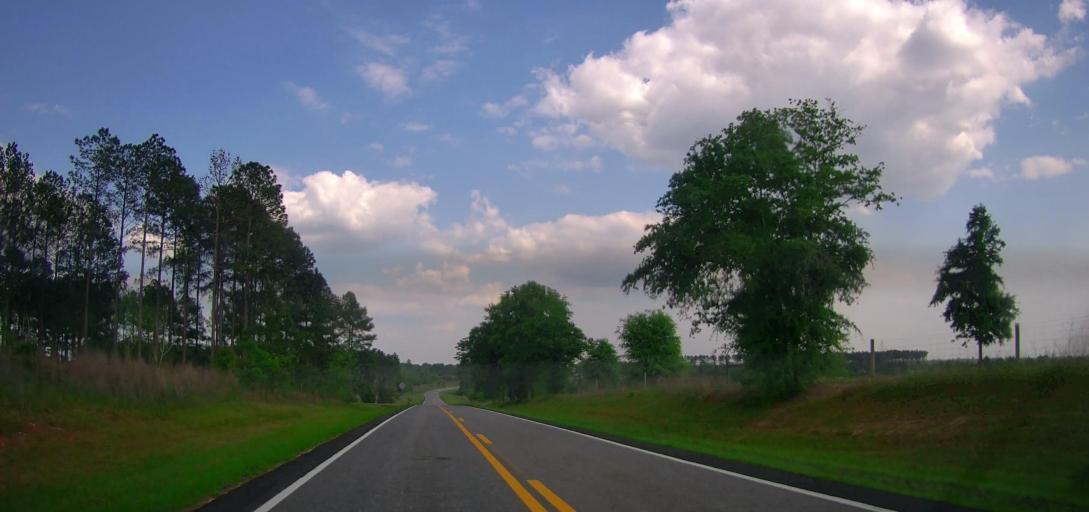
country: US
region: Georgia
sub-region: Laurens County
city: East Dublin
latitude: 32.6255
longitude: -82.8842
